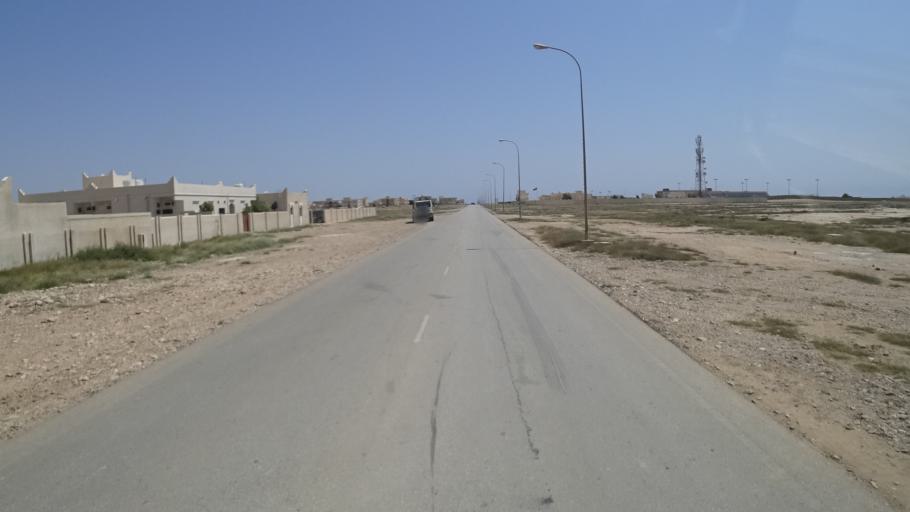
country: OM
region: Zufar
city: Salalah
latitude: 16.9865
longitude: 54.6984
